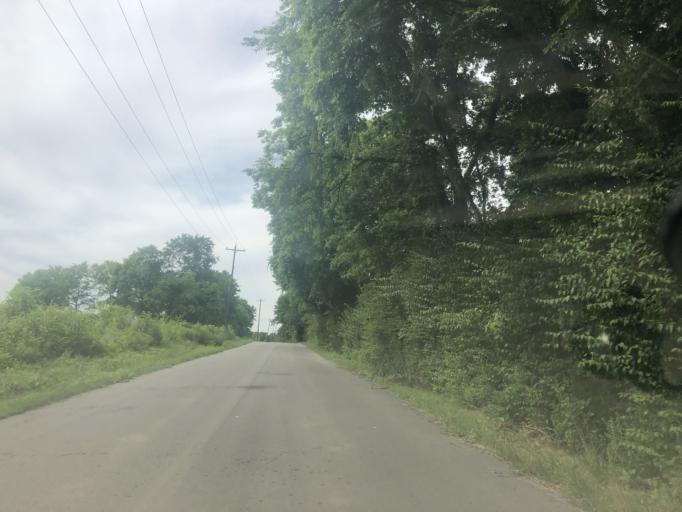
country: US
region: Tennessee
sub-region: Davidson County
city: Lakewood
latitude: 36.2188
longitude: -86.6533
